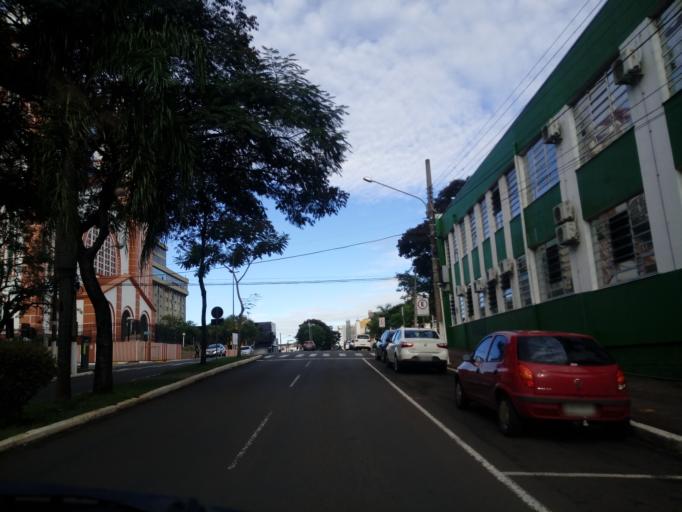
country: BR
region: Santa Catarina
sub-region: Chapeco
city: Chapeco
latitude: -27.1045
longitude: -52.6131
